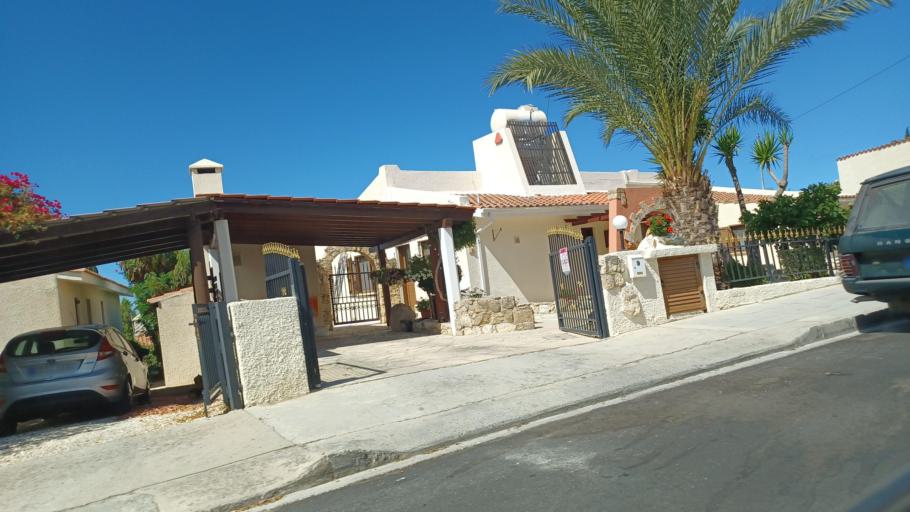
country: CY
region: Pafos
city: Tala
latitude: 34.8480
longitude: 32.4305
